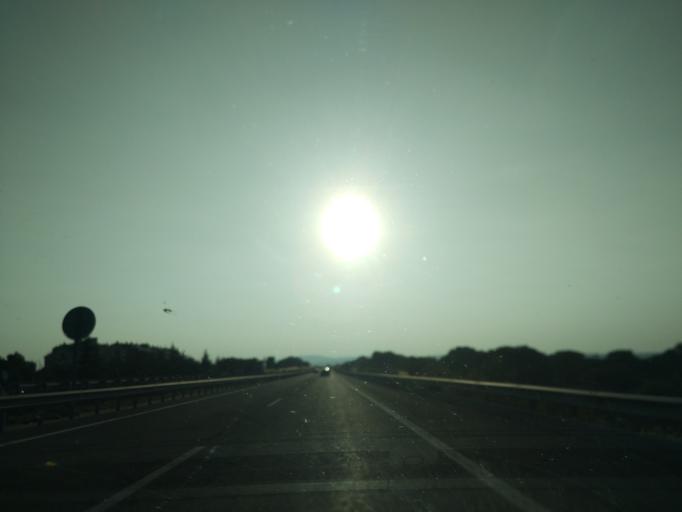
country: ES
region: Castille and Leon
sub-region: Provincia de Avila
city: Avila
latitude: 40.6709
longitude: -4.6586
